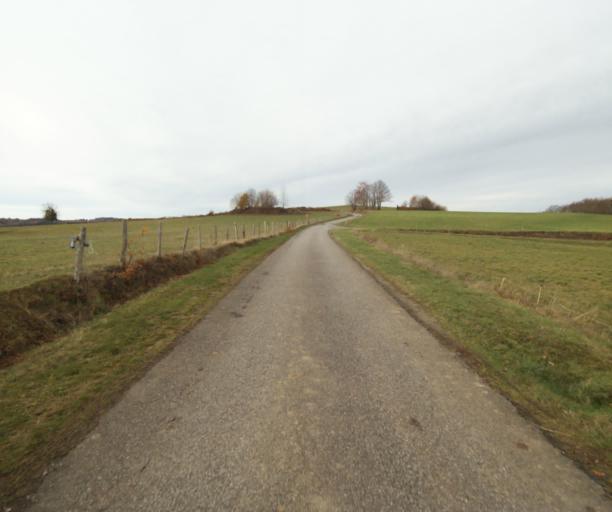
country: FR
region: Limousin
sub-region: Departement de la Correze
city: Sainte-Fortunade
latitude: 45.1619
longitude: 1.8100
